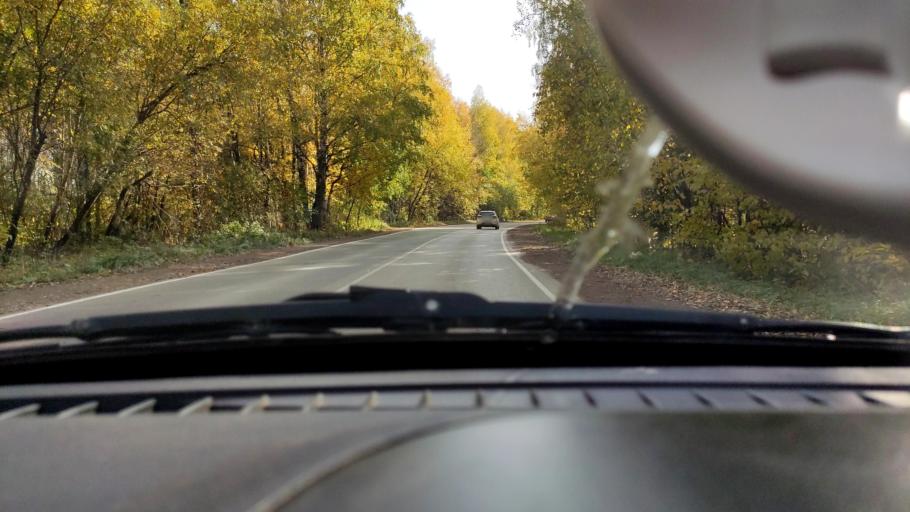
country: RU
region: Perm
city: Overyata
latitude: 58.0547
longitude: 55.8814
